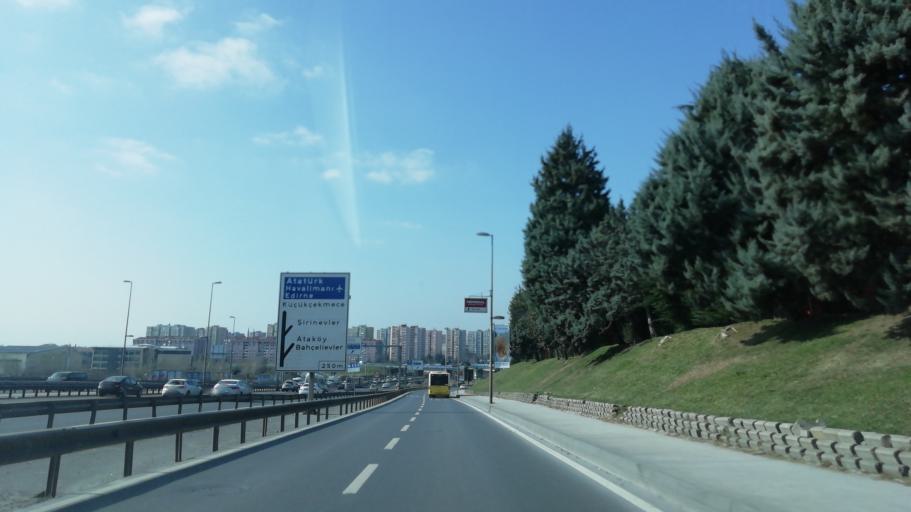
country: TR
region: Istanbul
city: Bahcelievler
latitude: 40.9933
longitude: 28.8568
